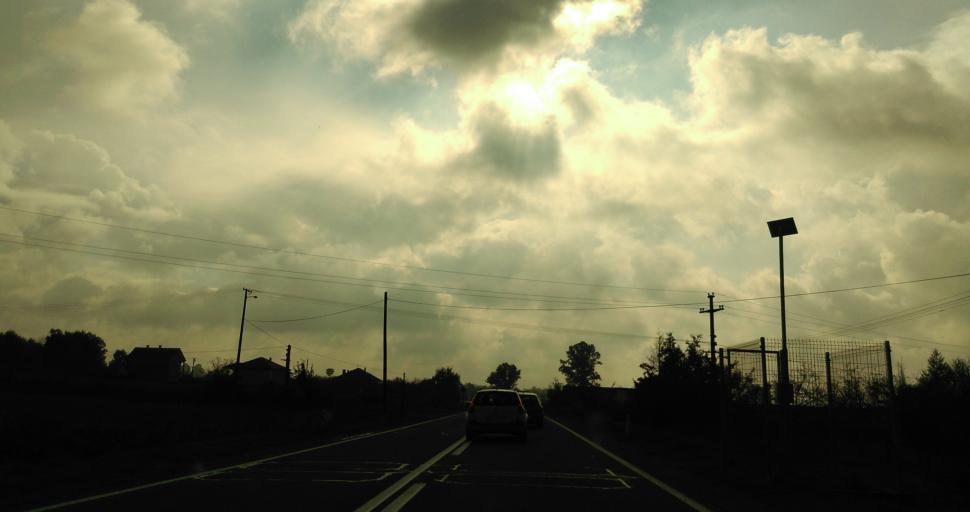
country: RS
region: Central Serbia
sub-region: Belgrade
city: Lazarevac
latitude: 44.3121
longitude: 20.2414
